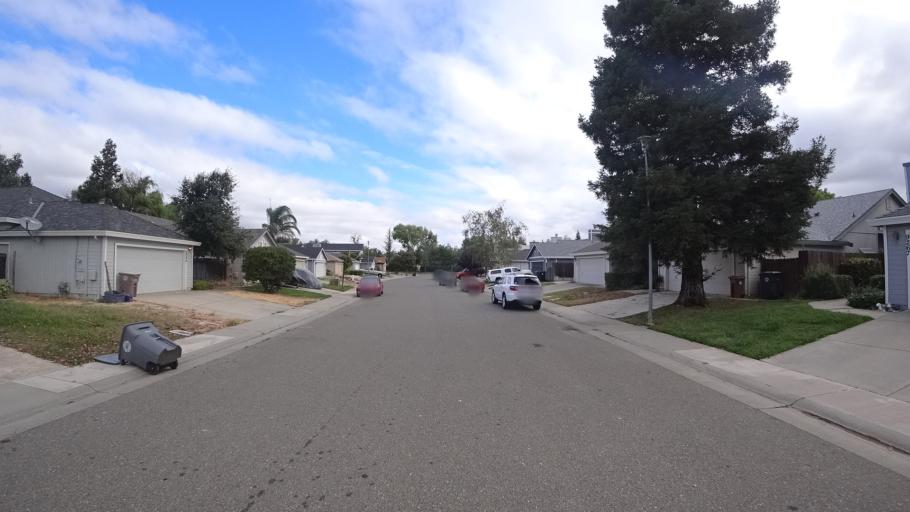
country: US
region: California
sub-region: Sacramento County
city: Laguna
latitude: 38.4206
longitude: -121.4269
